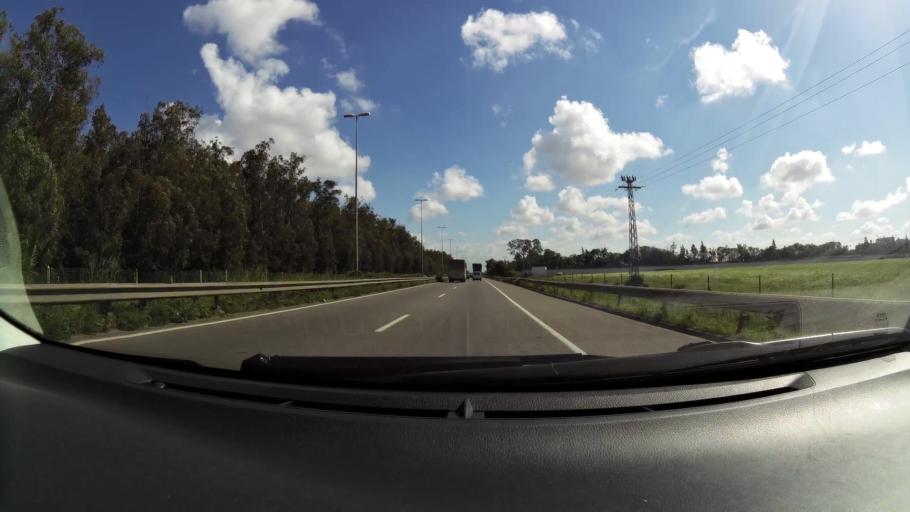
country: MA
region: Grand Casablanca
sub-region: Nouaceur
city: Bouskoura
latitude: 33.4746
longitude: -7.6334
